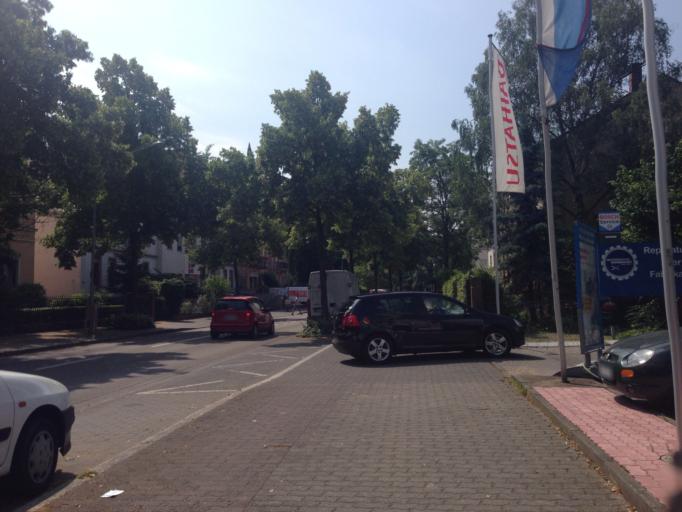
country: DE
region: Hesse
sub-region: Regierungsbezirk Darmstadt
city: Hanau am Main
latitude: 50.1418
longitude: 8.9113
